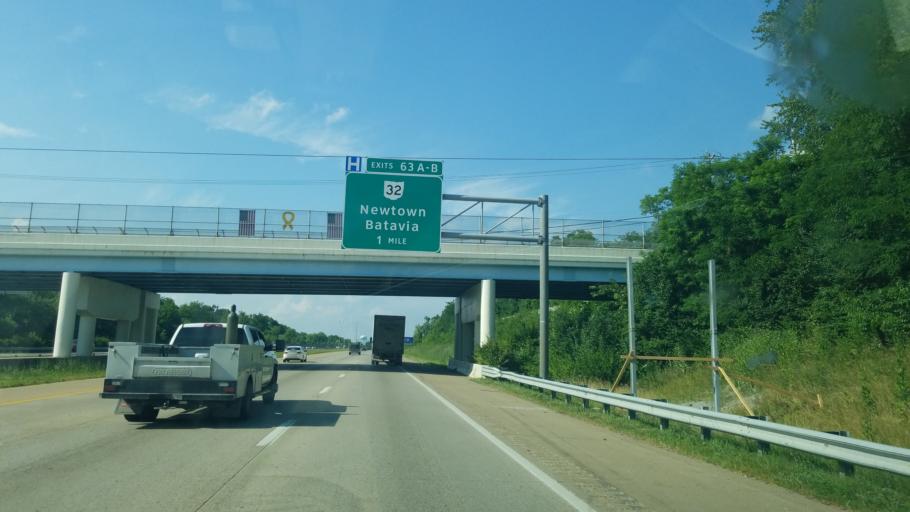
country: US
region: Ohio
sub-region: Clermont County
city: Summerside
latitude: 39.0846
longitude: -84.2897
